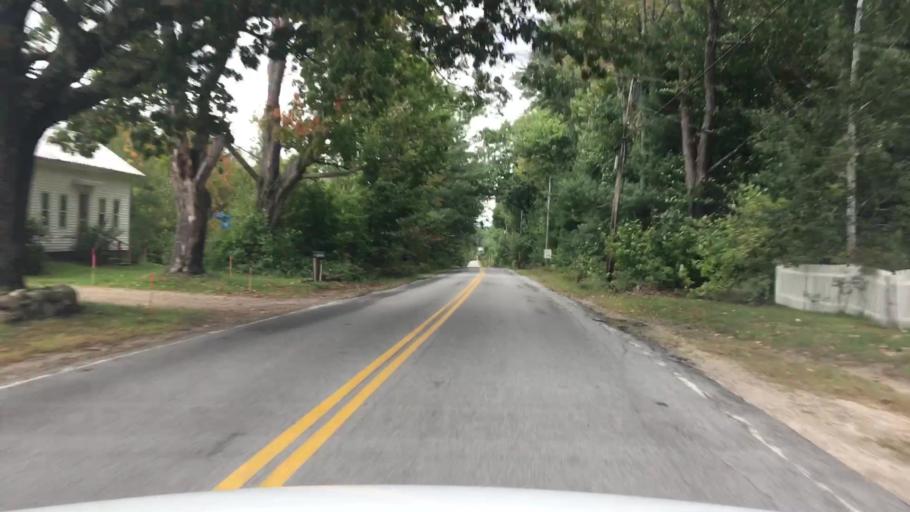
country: US
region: Maine
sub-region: York County
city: Parsonsfield
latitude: 43.7022
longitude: -70.9818
